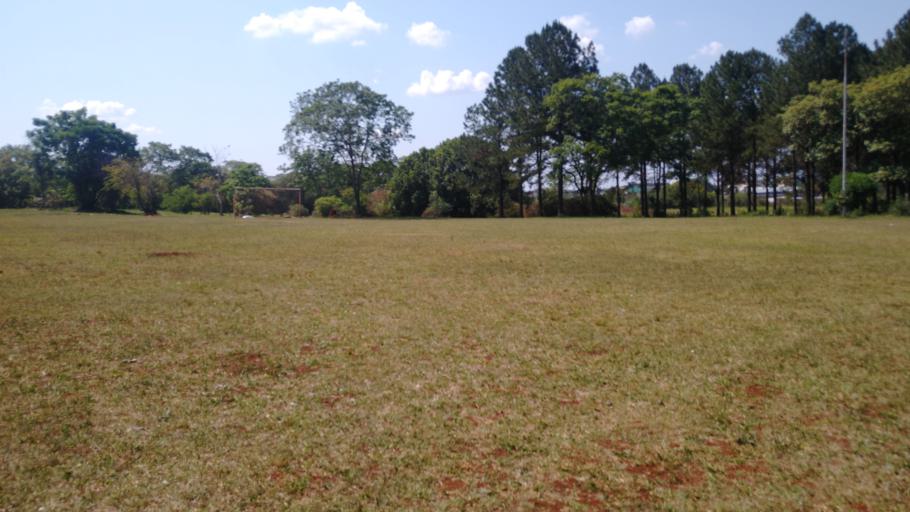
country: AR
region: Misiones
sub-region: Departamento de Capital
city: Posadas
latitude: -27.4052
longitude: -55.9686
